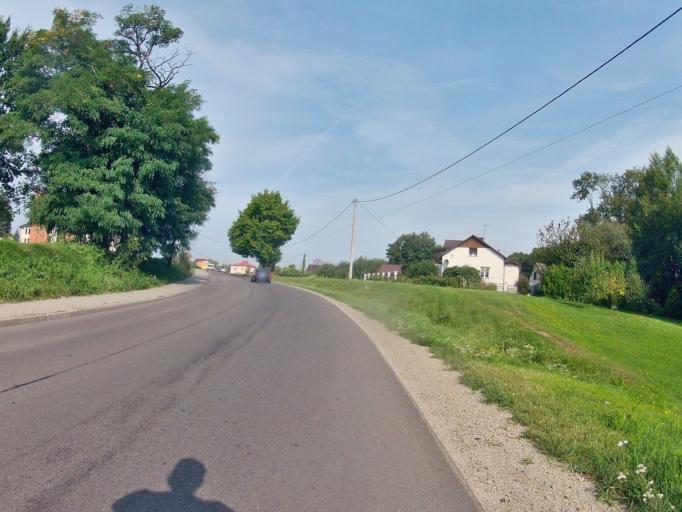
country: PL
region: Subcarpathian Voivodeship
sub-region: Powiat jasielski
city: Trzcinica
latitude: 49.7730
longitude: 21.4109
